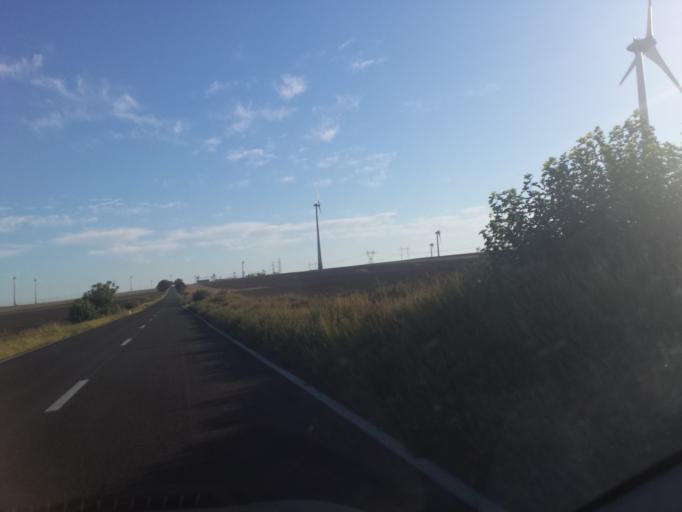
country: RO
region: Constanta
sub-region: Comuna Saraiu
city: Saraiu
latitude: 44.7862
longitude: 28.2328
